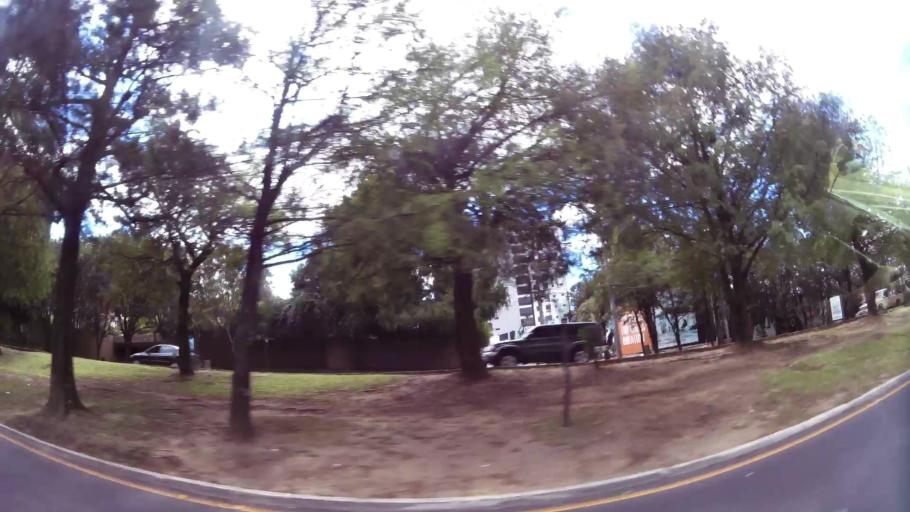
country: GT
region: Guatemala
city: Santa Catarina Pinula
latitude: 14.5820
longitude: -90.4851
